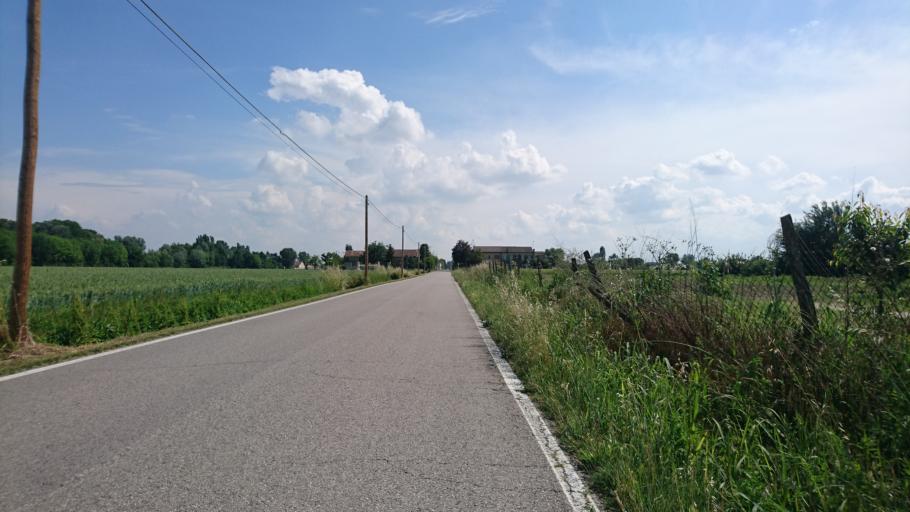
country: IT
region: Veneto
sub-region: Provincia di Rovigo
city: Castelmassa
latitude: 45.0388
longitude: 11.3132
